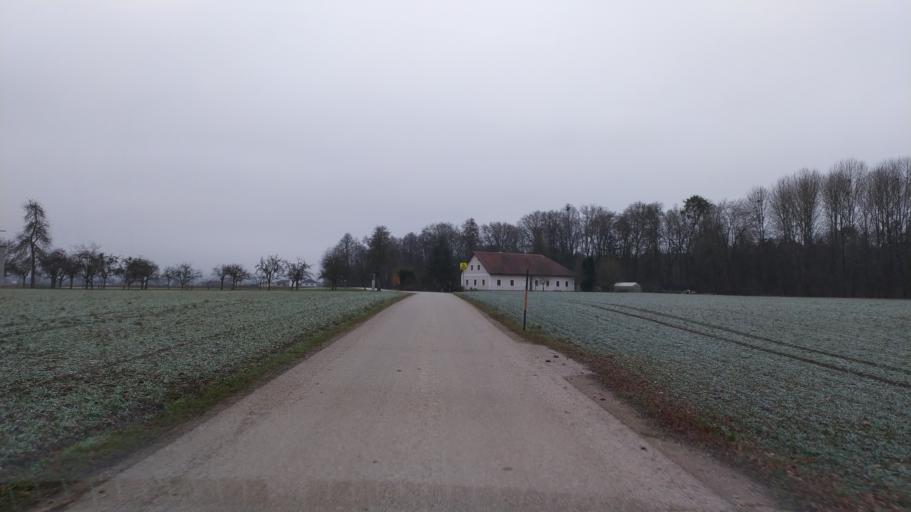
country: AT
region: Upper Austria
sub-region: Politischer Bezirk Perg
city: Perg
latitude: 48.2115
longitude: 14.7183
